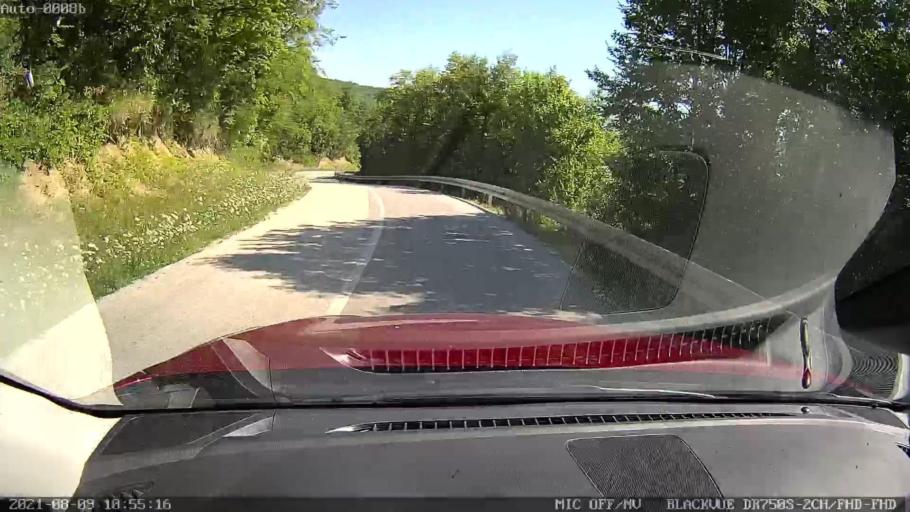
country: HR
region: Istarska
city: Pazin
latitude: 45.2838
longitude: 14.0763
